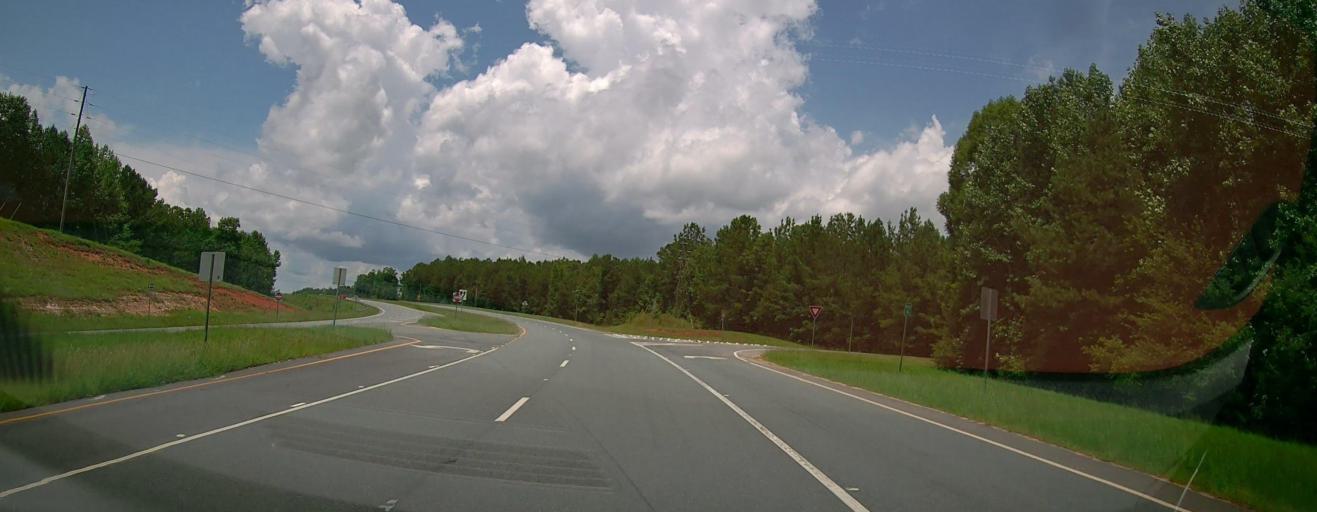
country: US
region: Georgia
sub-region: Upson County
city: Thomaston
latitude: 32.7877
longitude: -84.2485
